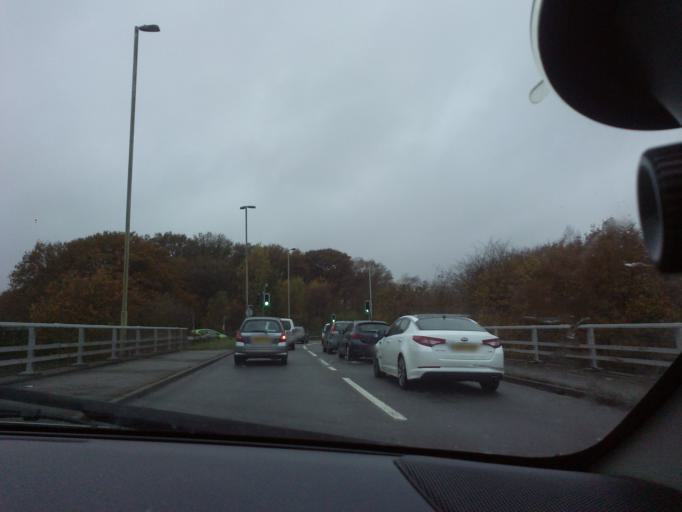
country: GB
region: England
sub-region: Hampshire
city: Hedge End
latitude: 50.9165
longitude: -1.3178
